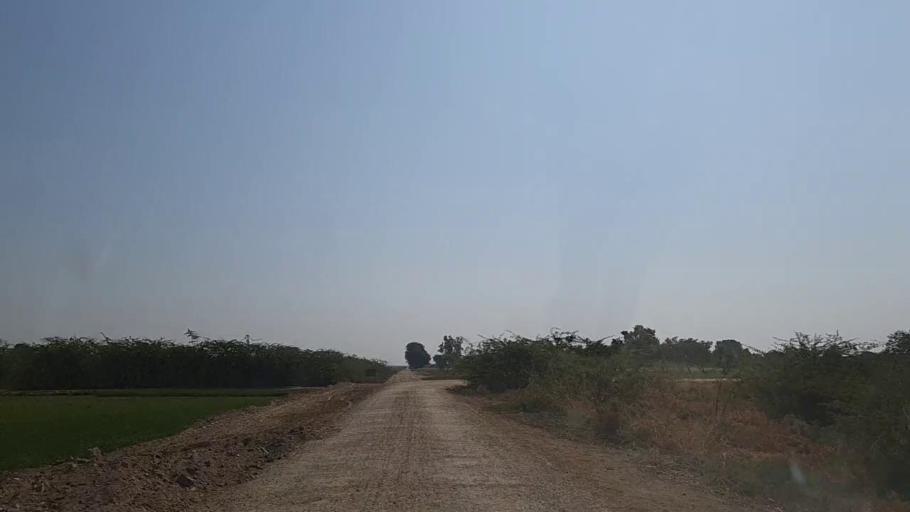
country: PK
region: Sindh
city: Digri
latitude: 24.9747
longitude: 69.2099
